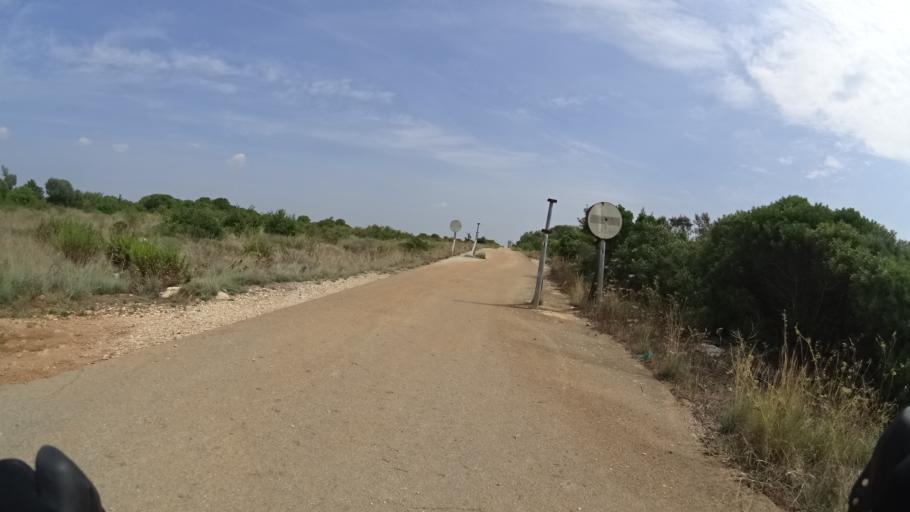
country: IT
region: Apulia
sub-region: Provincia di Brindisi
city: San Pancrazio Salentino
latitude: 40.3471
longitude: 17.8174
